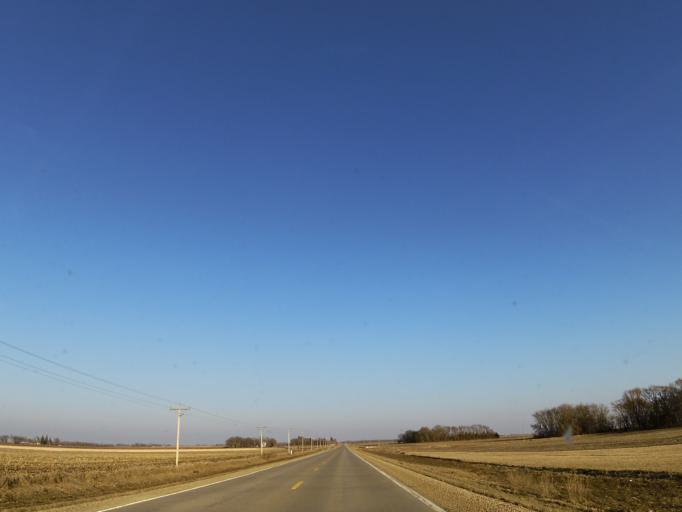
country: US
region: Iowa
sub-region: Worth County
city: Northwood
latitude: 43.4372
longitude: -93.1001
